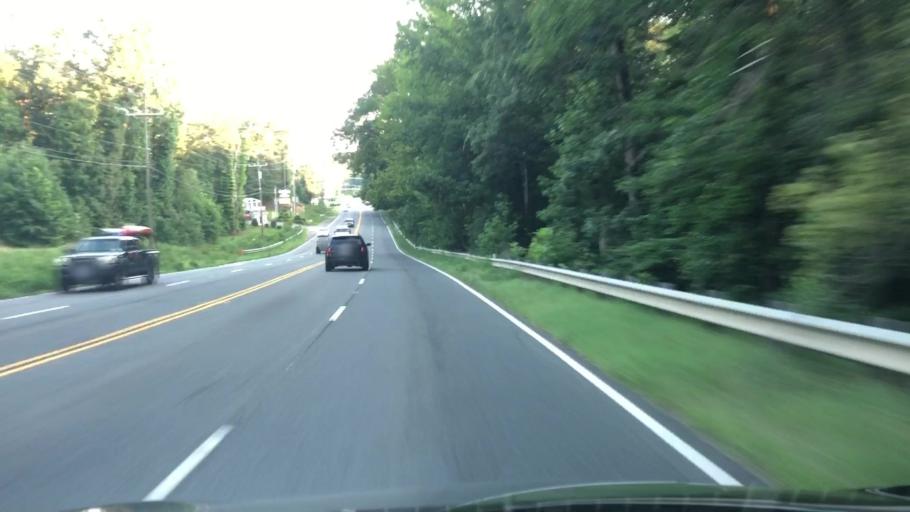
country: US
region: Virginia
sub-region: Stafford County
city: Falmouth
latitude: 38.3563
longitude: -77.4584
